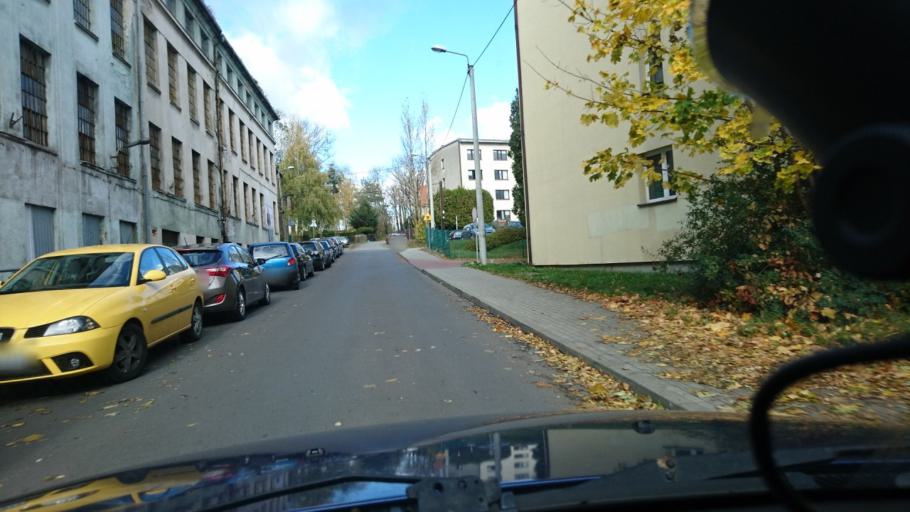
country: PL
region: Silesian Voivodeship
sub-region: Bielsko-Biala
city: Bielsko-Biala
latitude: 49.8333
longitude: 19.0402
